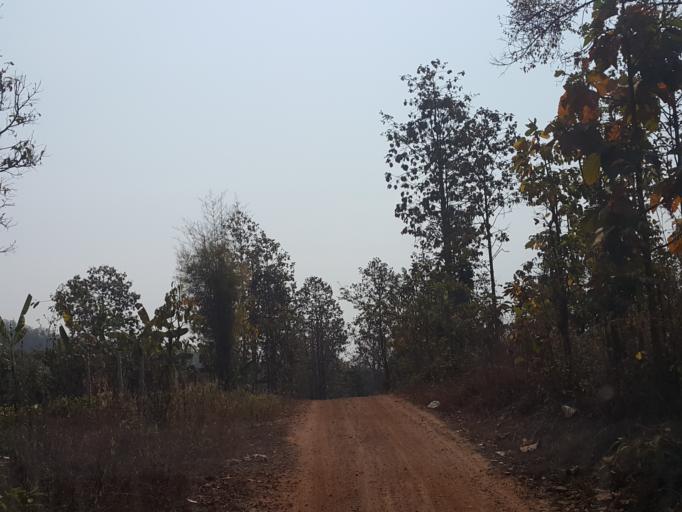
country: TH
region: Chiang Mai
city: Hang Dong
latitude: 18.7239
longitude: 98.8551
